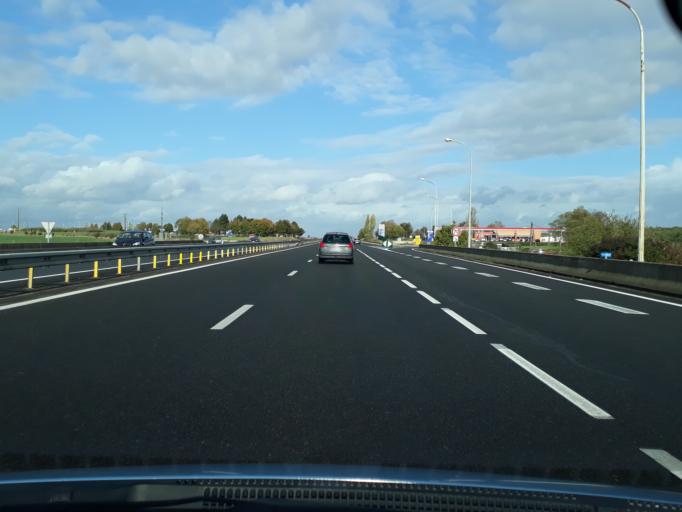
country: FR
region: Centre
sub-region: Departement du Loir-et-Cher
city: La Chaussee-Saint-Victor
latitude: 47.6608
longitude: 1.3843
